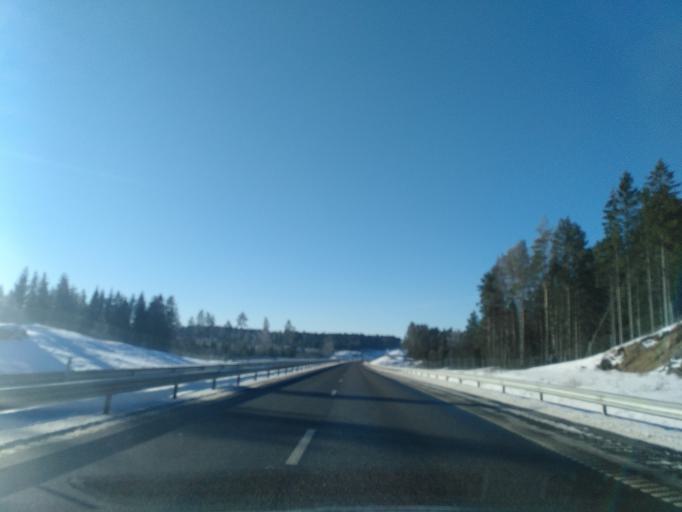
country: SE
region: Vaestra Goetaland
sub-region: Vargarda Kommun
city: Jonstorp
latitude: 57.9847
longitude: 12.7180
